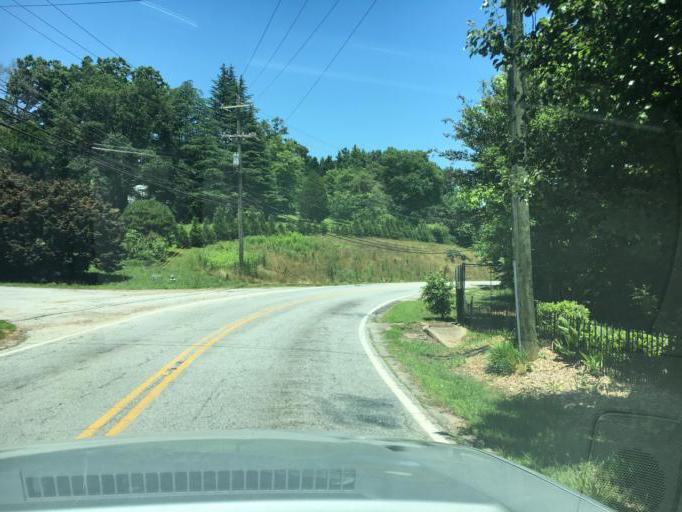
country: US
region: South Carolina
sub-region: Greenville County
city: Greer
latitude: 34.9586
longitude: -82.2084
